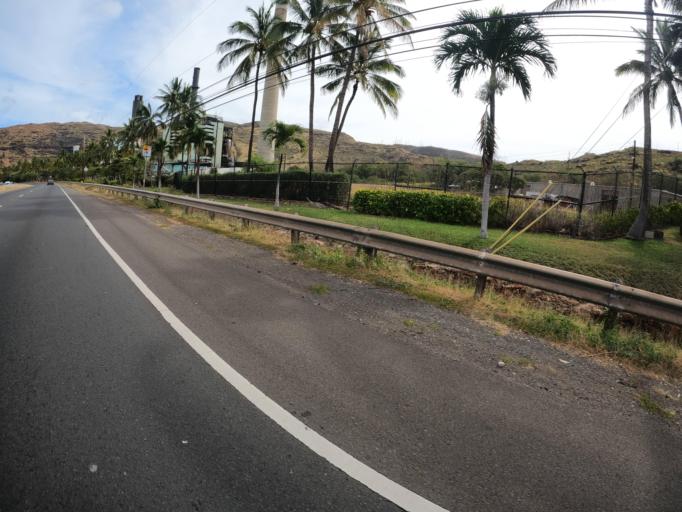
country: US
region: Hawaii
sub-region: Honolulu County
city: Makakilo
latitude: 21.3534
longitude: -158.1287
